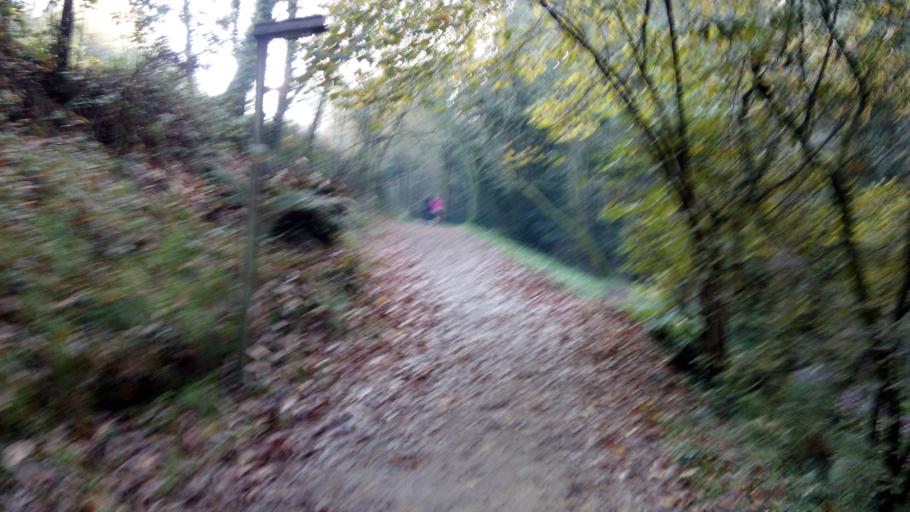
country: ES
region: Galicia
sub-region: Provincia de Pontevedra
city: Meis
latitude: 42.4879
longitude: -8.7521
